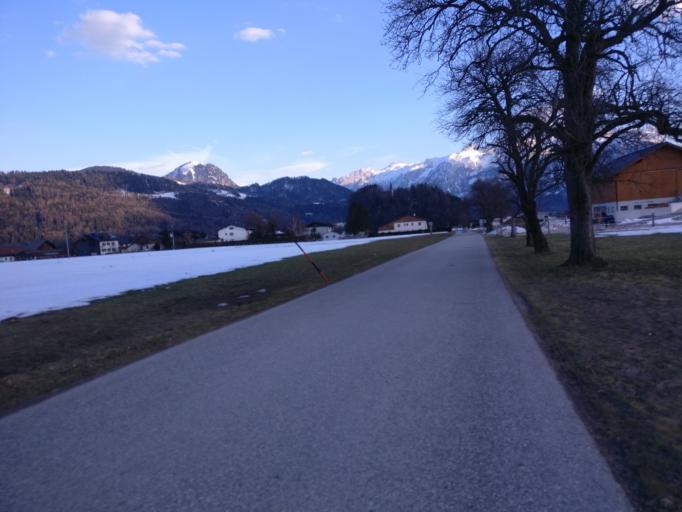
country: AT
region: Salzburg
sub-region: Politischer Bezirk Hallein
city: Kuchl
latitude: 47.6422
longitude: 13.1515
